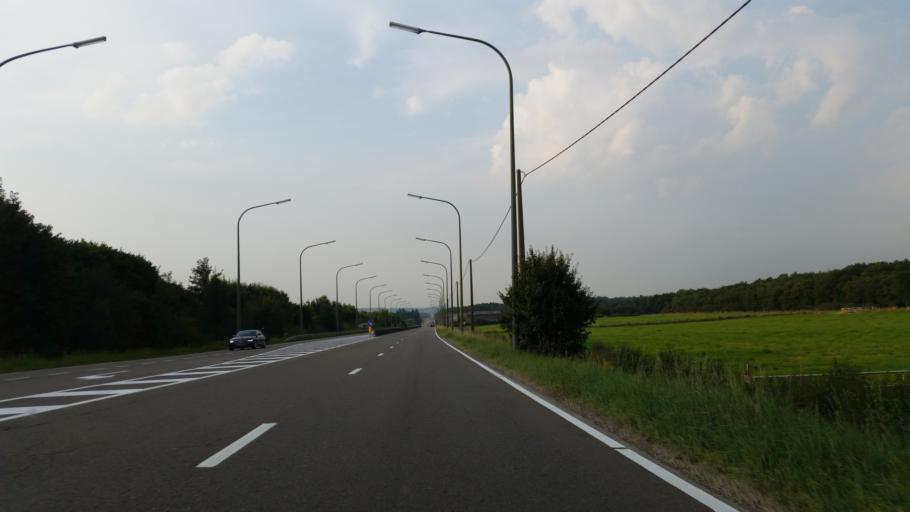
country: BE
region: Wallonia
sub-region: Province du Luxembourg
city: Marche-en-Famenne
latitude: 50.2431
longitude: 5.3453
